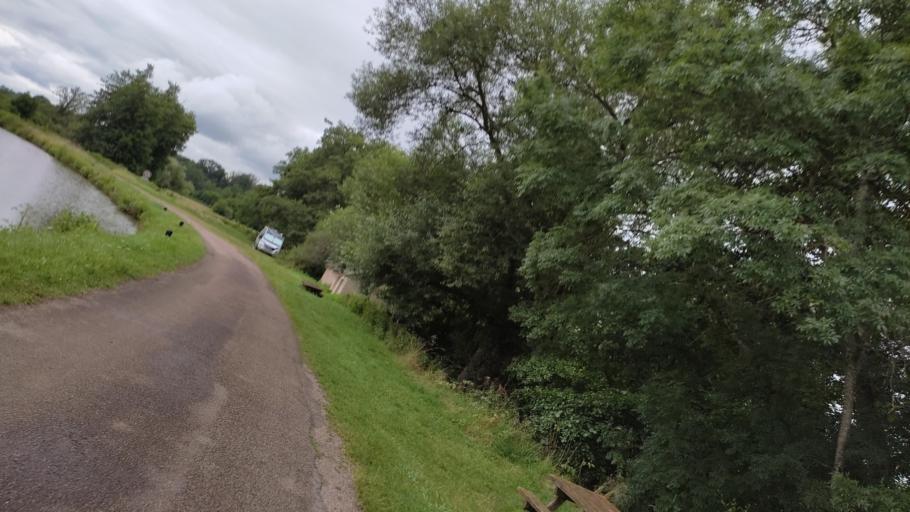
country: FR
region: Bourgogne
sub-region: Departement de la Nievre
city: Corbigny
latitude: 47.2782
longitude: 3.6566
